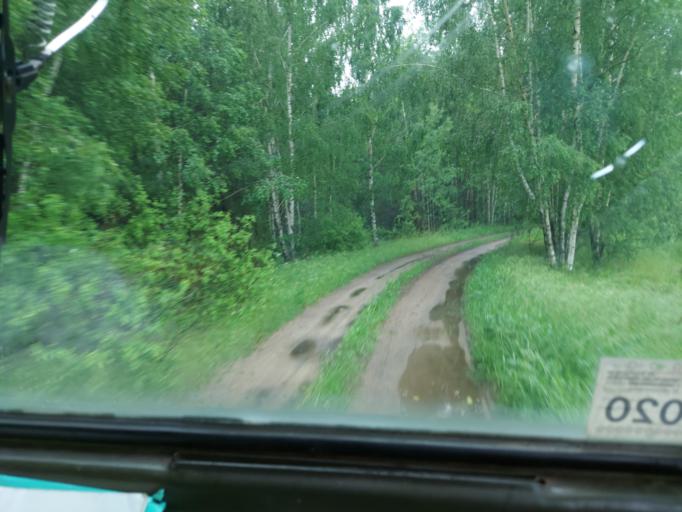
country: BY
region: Mogilev
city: Poselok Voskhod
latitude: 53.6732
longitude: 30.4031
